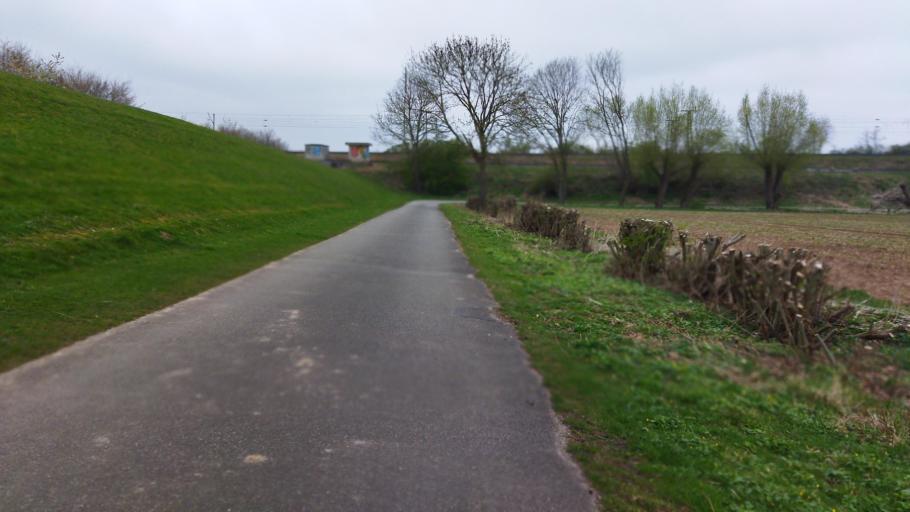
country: DE
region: Lower Saxony
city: Riede
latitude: 53.0271
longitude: 8.8874
